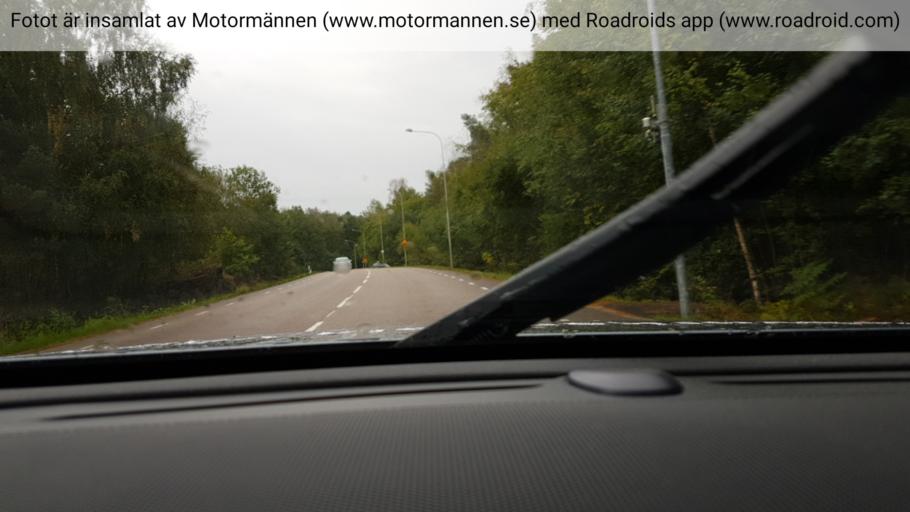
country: SE
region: Vaestra Goetaland
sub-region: Vanersborgs Kommun
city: Vanersborg
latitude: 58.3473
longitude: 12.3490
